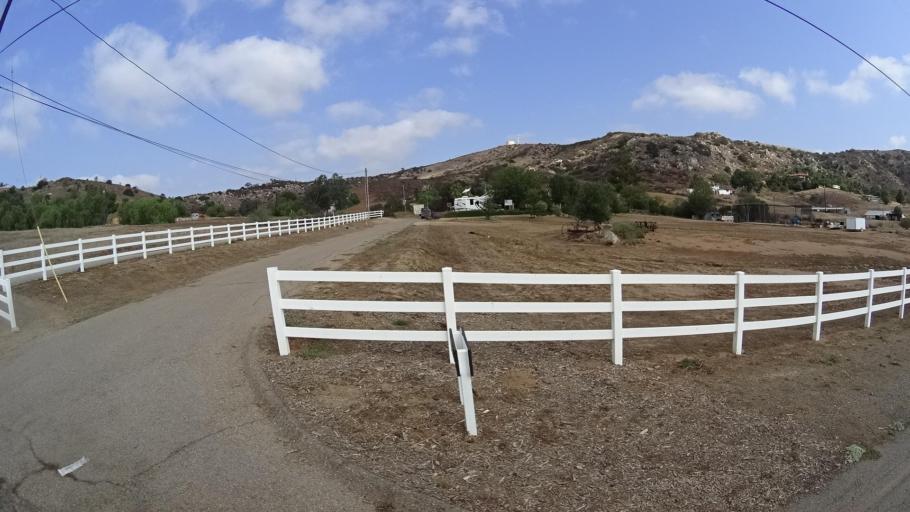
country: US
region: California
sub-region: San Diego County
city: Ramona
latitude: 33.0289
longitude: -116.8373
